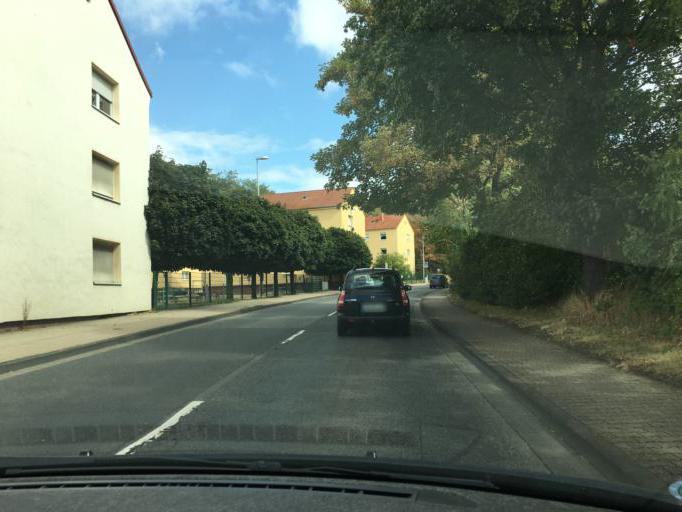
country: DE
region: North Rhine-Westphalia
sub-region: Regierungsbezirk Koln
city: Dueren
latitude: 50.8131
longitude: 6.4831
